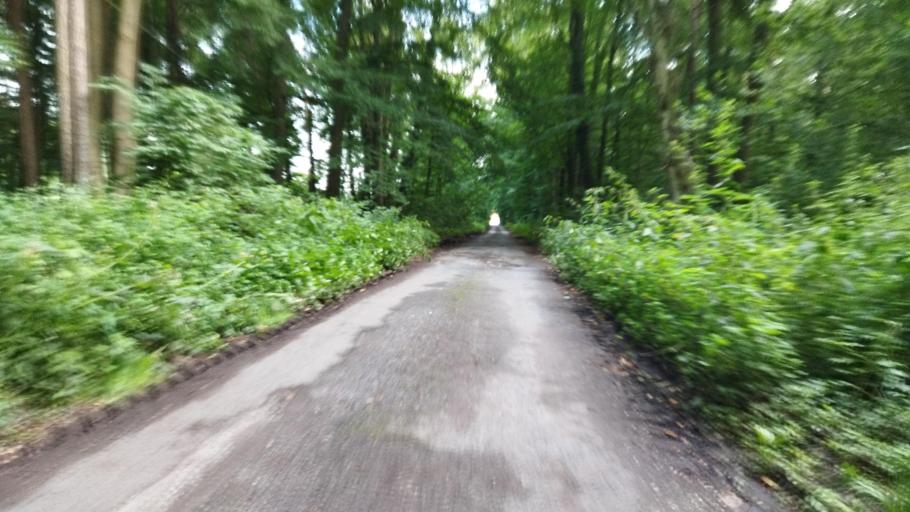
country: DE
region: Lower Saxony
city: Glandorf
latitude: 52.0901
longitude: 8.0347
